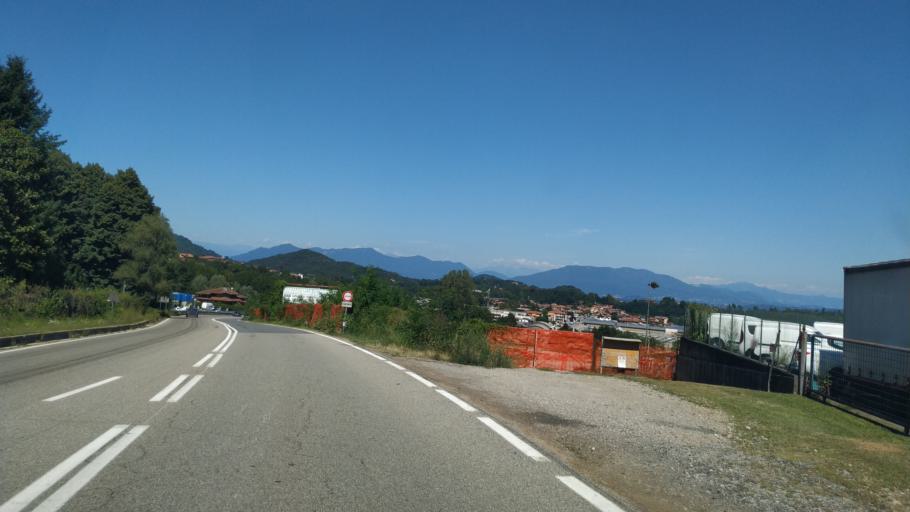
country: IT
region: Piedmont
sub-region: Provincia di Novara
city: Paruzzaro
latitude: 45.7396
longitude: 8.5116
